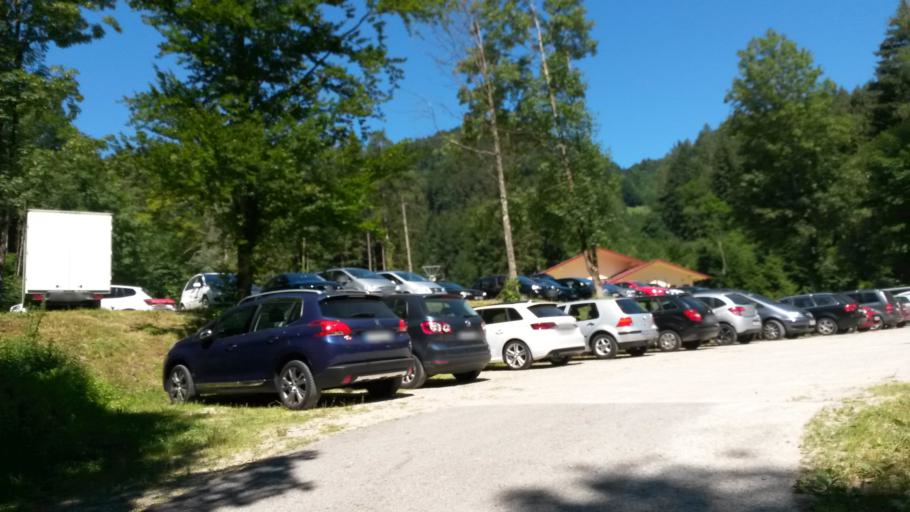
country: DE
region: Bavaria
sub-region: Upper Bavaria
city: Marquartstein
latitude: 47.7608
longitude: 12.4357
